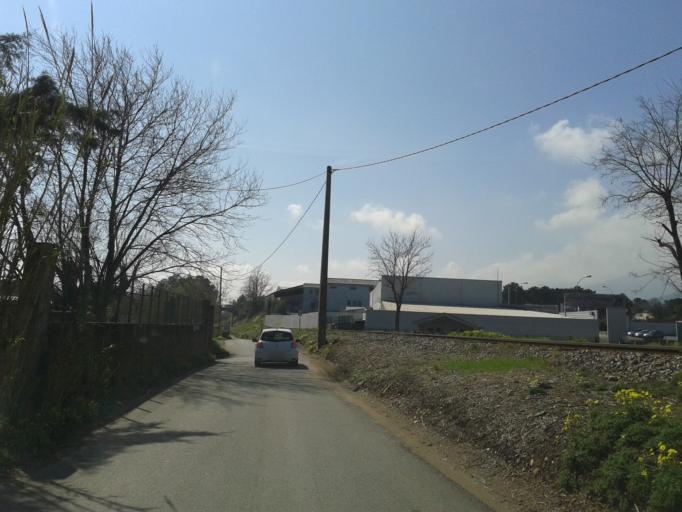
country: FR
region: Corsica
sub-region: Departement de la Haute-Corse
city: Biguglia
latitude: 42.6507
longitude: 9.4412
